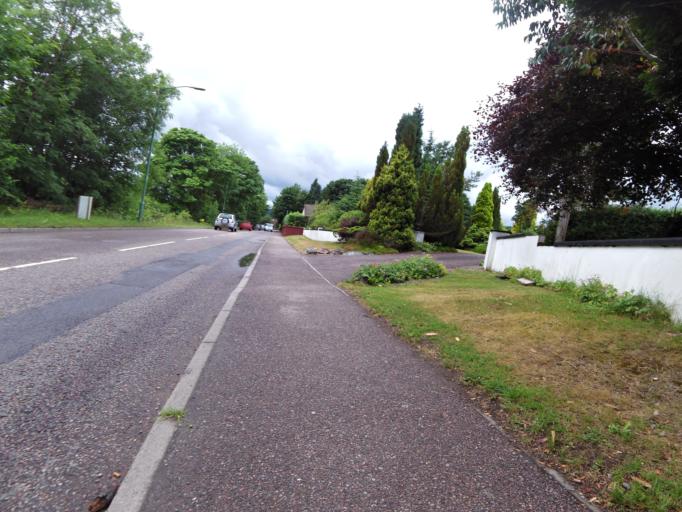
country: GB
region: Scotland
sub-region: Highland
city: Fort William
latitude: 56.8346
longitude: -5.0883
